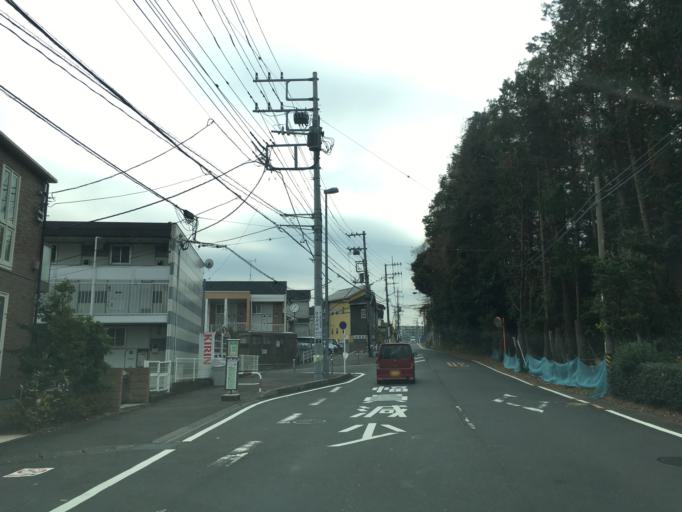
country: JP
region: Kanagawa
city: Minami-rinkan
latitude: 35.5097
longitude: 139.4639
